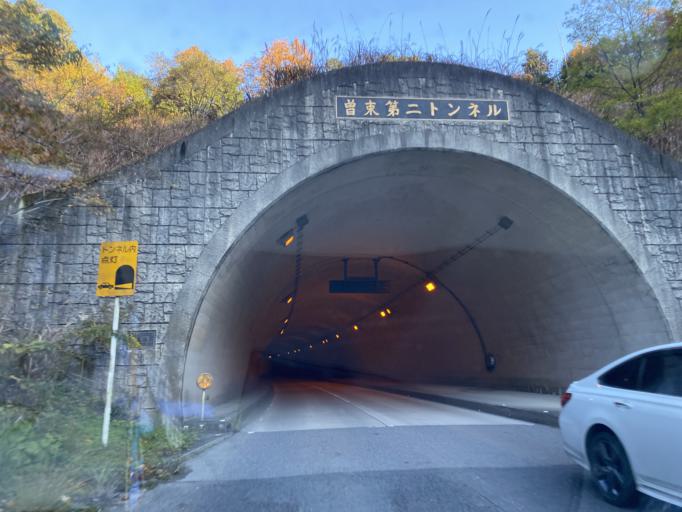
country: JP
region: Kyoto
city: Uji
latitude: 34.9022
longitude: 135.8827
